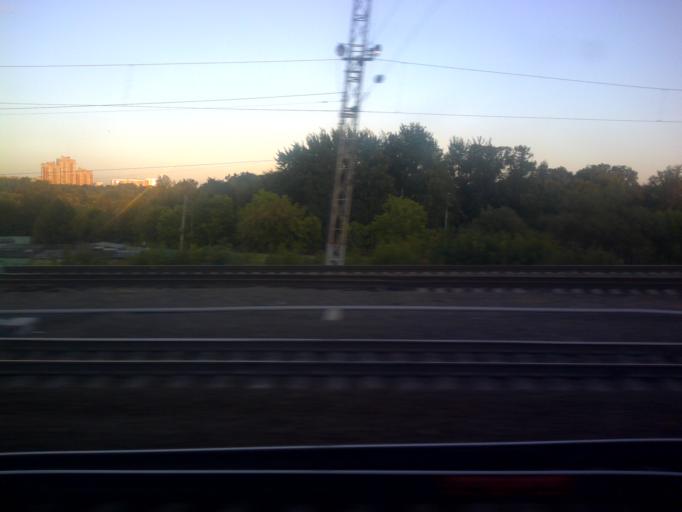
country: RU
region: Moscow
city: Orekhovo-Borisovo Severnoye
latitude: 55.6225
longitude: 37.6745
